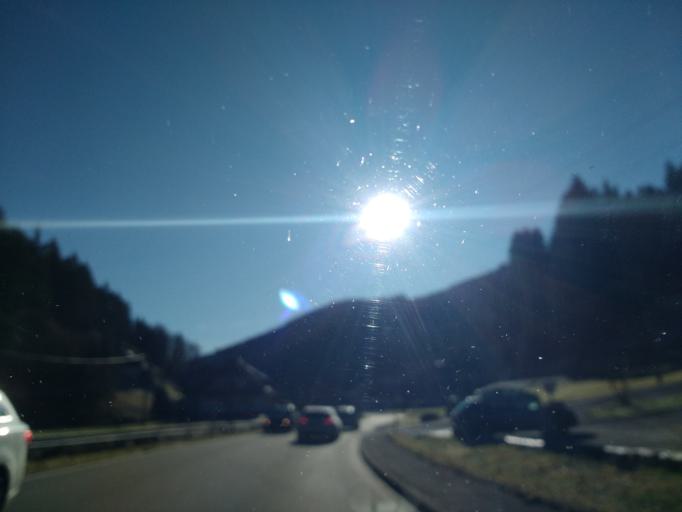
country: DE
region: Baden-Wuerttemberg
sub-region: Karlsruhe Region
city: Bad Rippoldsau-Schapbach
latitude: 48.4404
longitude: 8.3145
